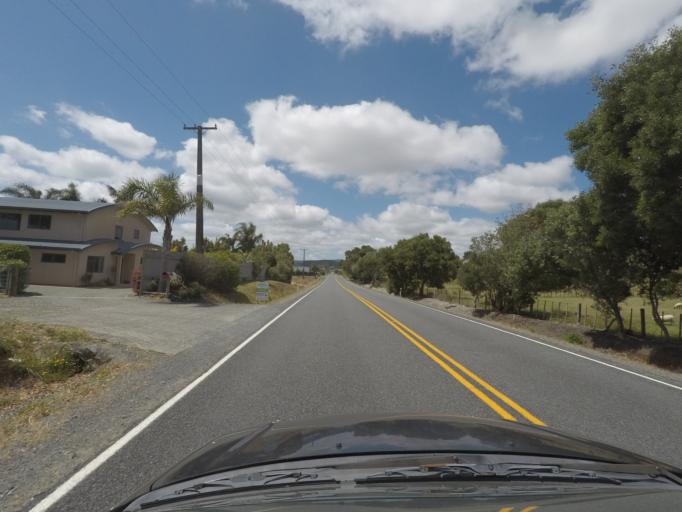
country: NZ
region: Northland
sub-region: Whangarei
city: Ruakaka
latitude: -36.0029
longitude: 174.4768
